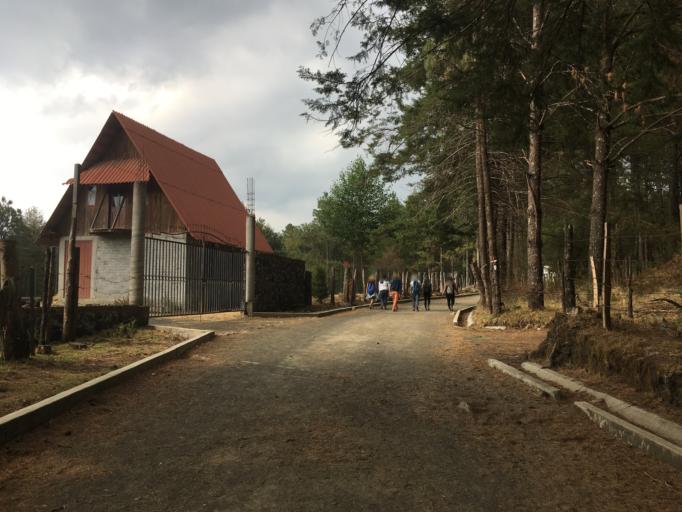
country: MX
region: Michoacan
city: Angahuan
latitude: 19.5377
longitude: -102.2424
